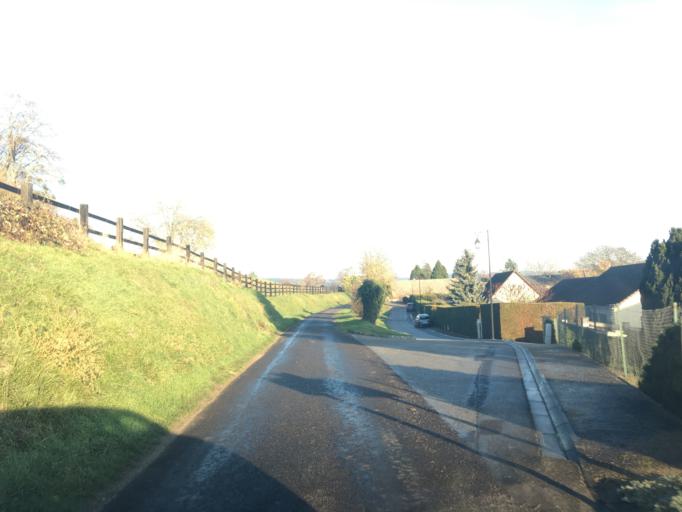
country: FR
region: Haute-Normandie
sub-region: Departement de l'Eure
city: Houlbec-Cocherel
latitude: 49.0523
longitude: 1.2964
